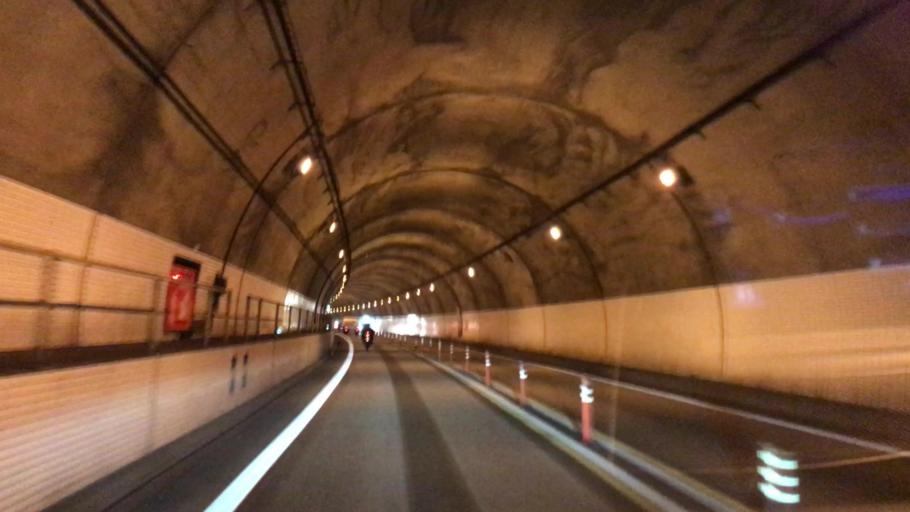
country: JP
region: Hokkaido
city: Chitose
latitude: 42.9180
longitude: 141.9501
